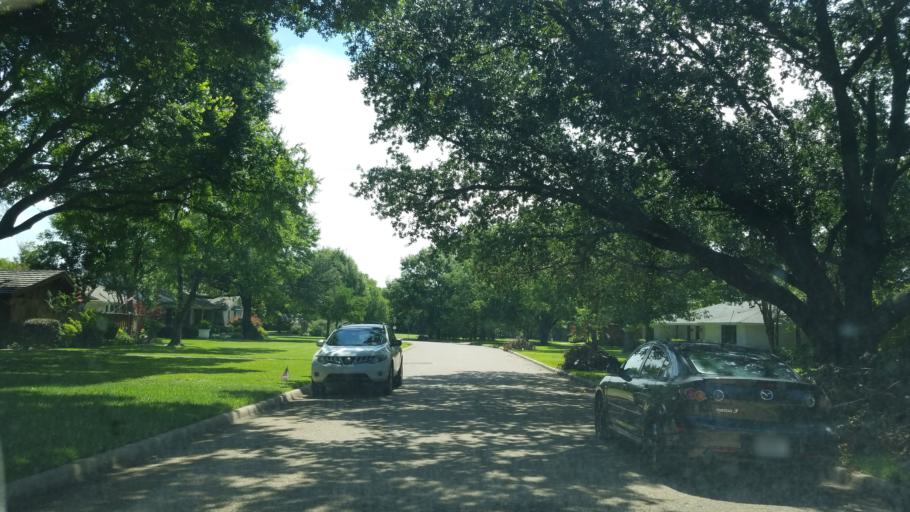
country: US
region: Texas
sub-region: Dallas County
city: Farmers Branch
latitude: 32.9080
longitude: -96.8479
